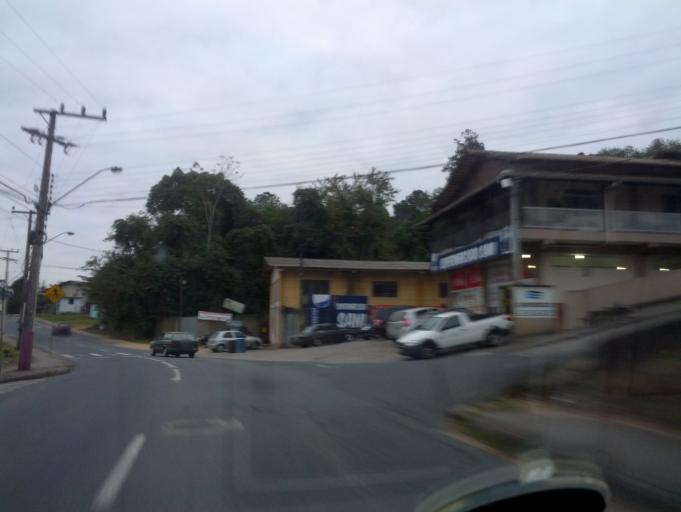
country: BR
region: Santa Catarina
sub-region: Blumenau
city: Blumenau
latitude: -26.8741
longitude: -49.0824
